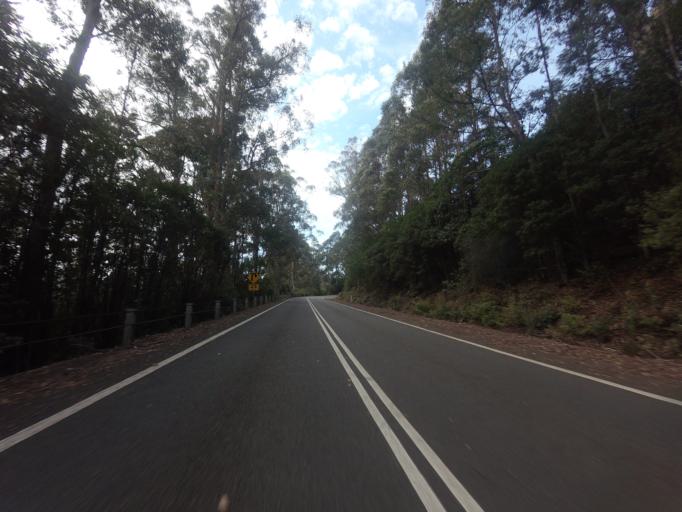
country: AU
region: Tasmania
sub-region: Meander Valley
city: Deloraine
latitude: -41.6514
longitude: 146.7221
